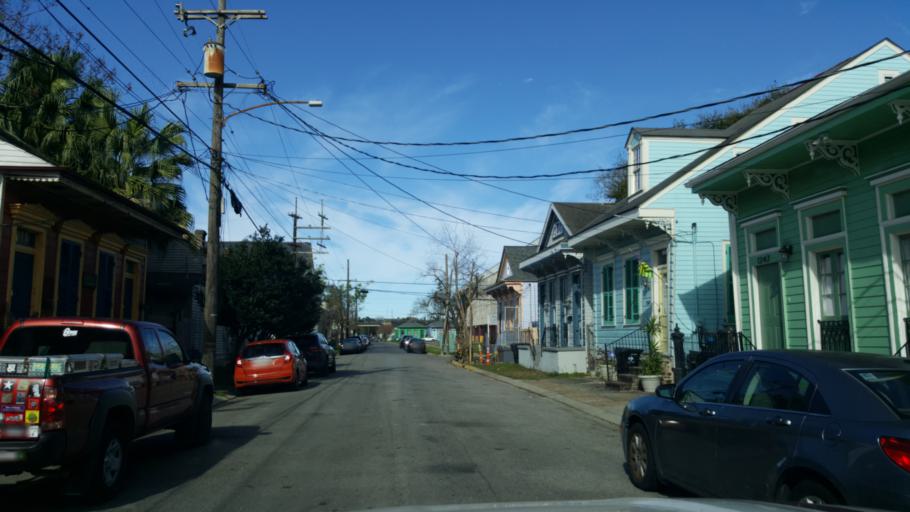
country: US
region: Louisiana
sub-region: Orleans Parish
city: New Orleans
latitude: 29.9679
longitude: -90.0646
